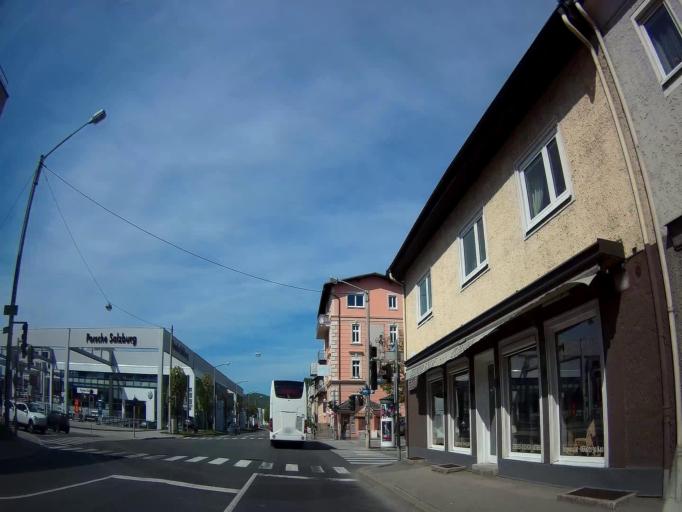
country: AT
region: Salzburg
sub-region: Salzburg Stadt
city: Salzburg
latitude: 47.8151
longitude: 13.0537
